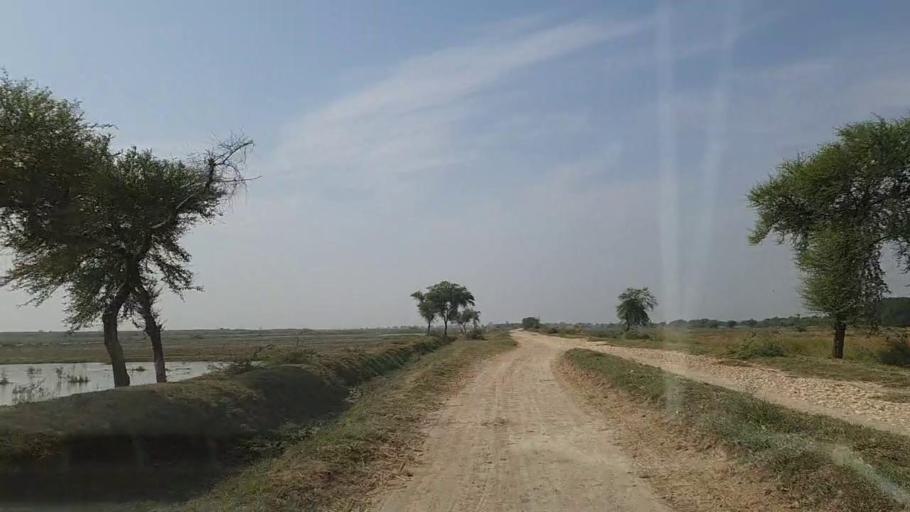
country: PK
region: Sindh
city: Mirpur Batoro
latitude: 24.6108
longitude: 68.2233
